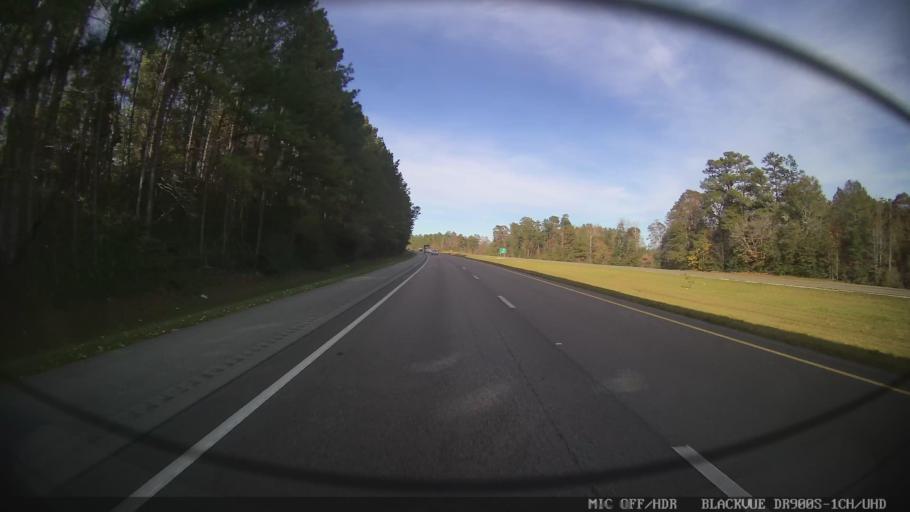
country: US
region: Mississippi
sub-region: Lamar County
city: West Hattiesburg
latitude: 31.2245
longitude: -89.3249
